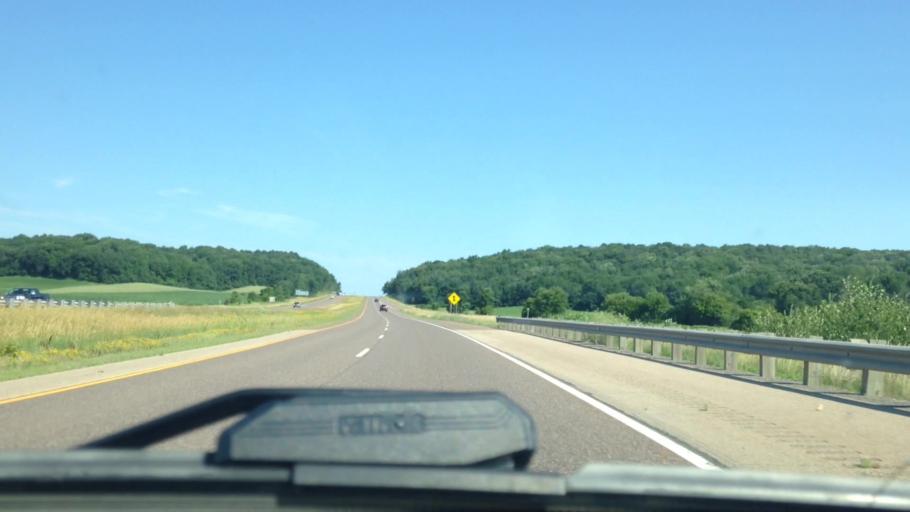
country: US
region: Wisconsin
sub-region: Chippewa County
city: Chippewa Falls
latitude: 44.9665
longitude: -91.4273
